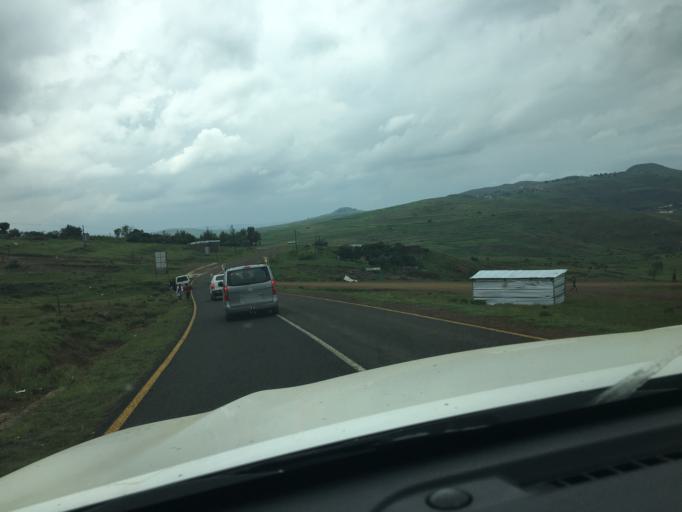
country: LS
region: Berea
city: Teyateyaneng
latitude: -29.2547
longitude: 27.8464
